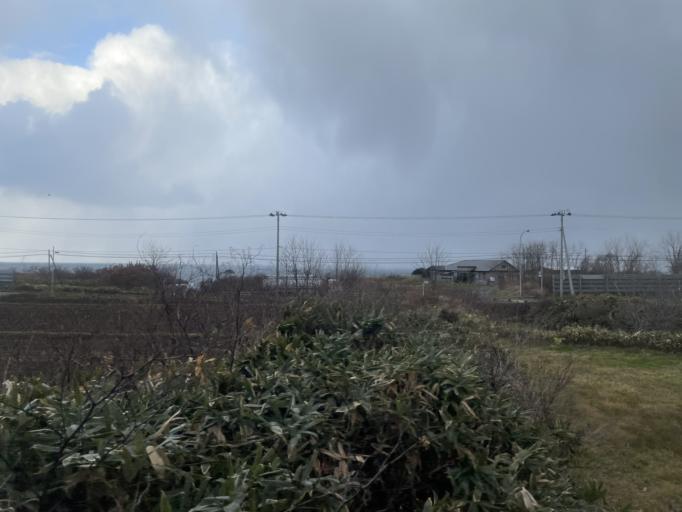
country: JP
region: Aomori
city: Mutsu
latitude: 41.1256
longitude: 141.2669
